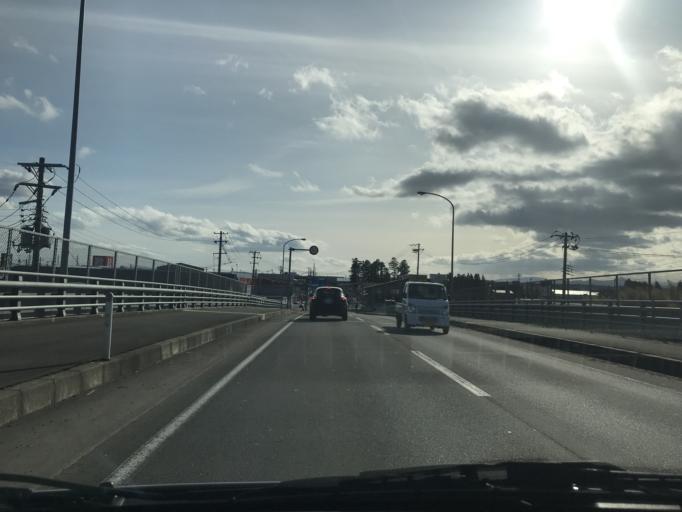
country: JP
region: Iwate
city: Kitakami
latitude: 39.2957
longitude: 141.0978
